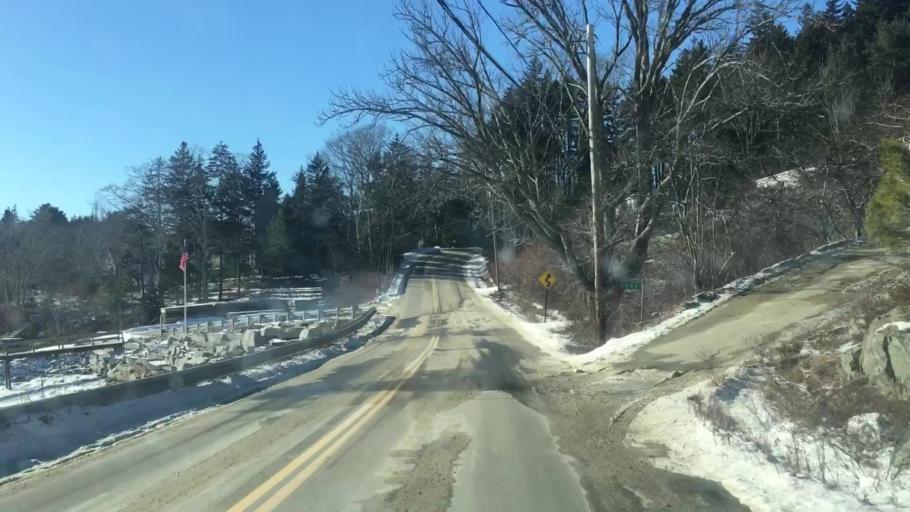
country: US
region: Maine
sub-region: Hancock County
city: Castine
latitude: 44.3421
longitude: -68.7407
